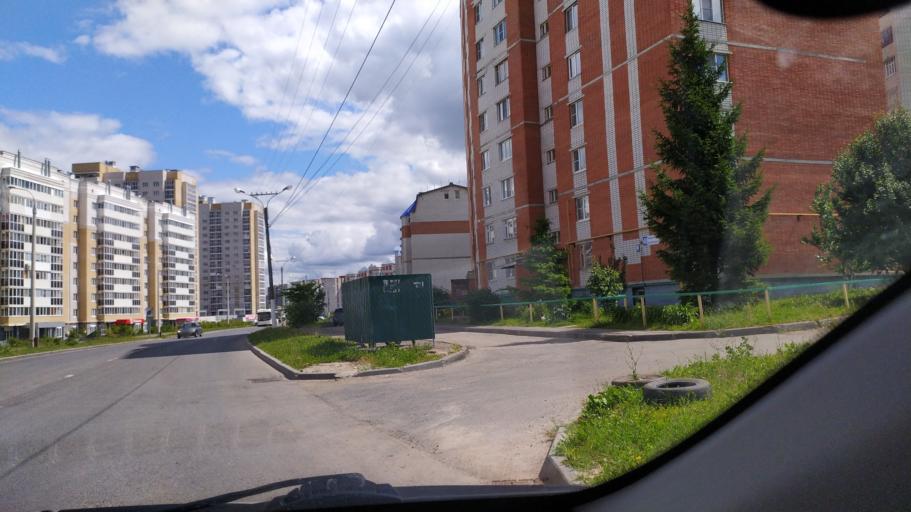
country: RU
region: Chuvashia
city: Novyye Lapsary
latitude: 56.1221
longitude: 47.1757
